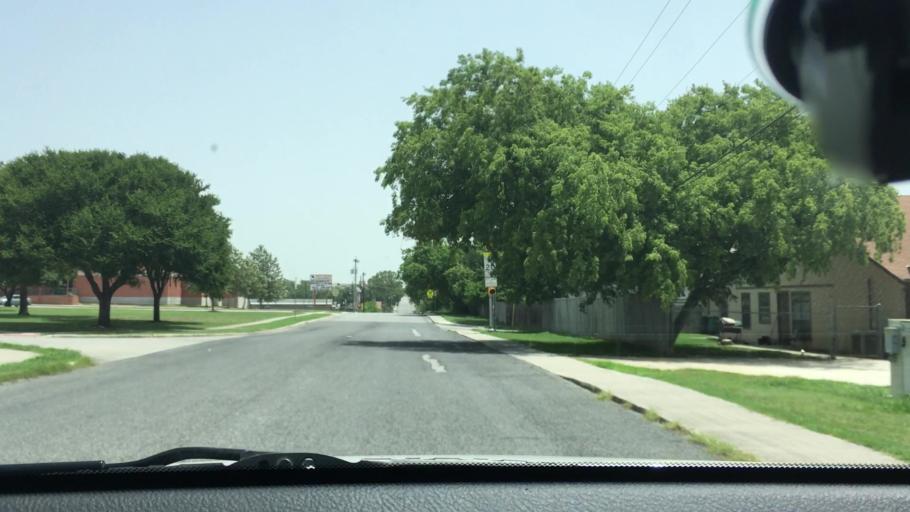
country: US
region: Texas
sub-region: Bexar County
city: Live Oak
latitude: 29.5744
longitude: -98.3685
